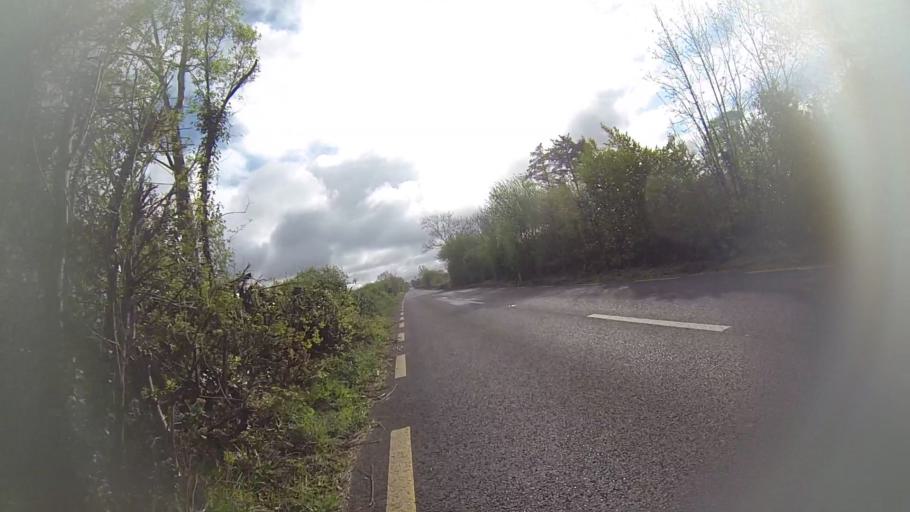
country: IE
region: Munster
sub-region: Ciarrai
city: Kenmare
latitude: 51.8803
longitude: -9.6141
